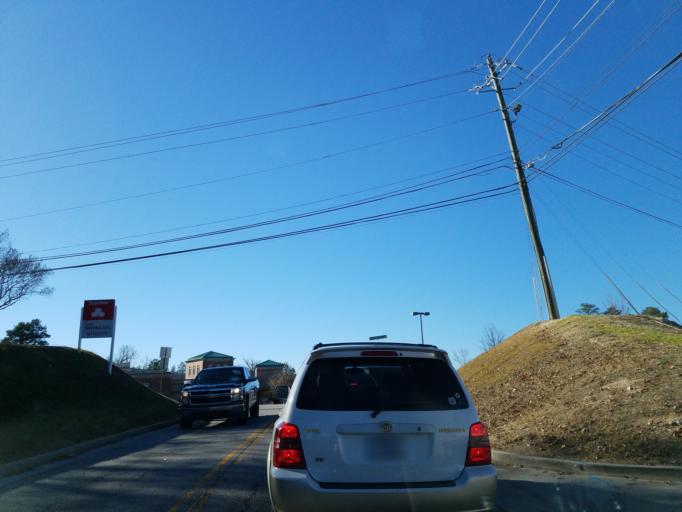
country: US
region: Georgia
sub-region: Cobb County
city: Vinings
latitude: 33.8271
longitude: -84.4949
